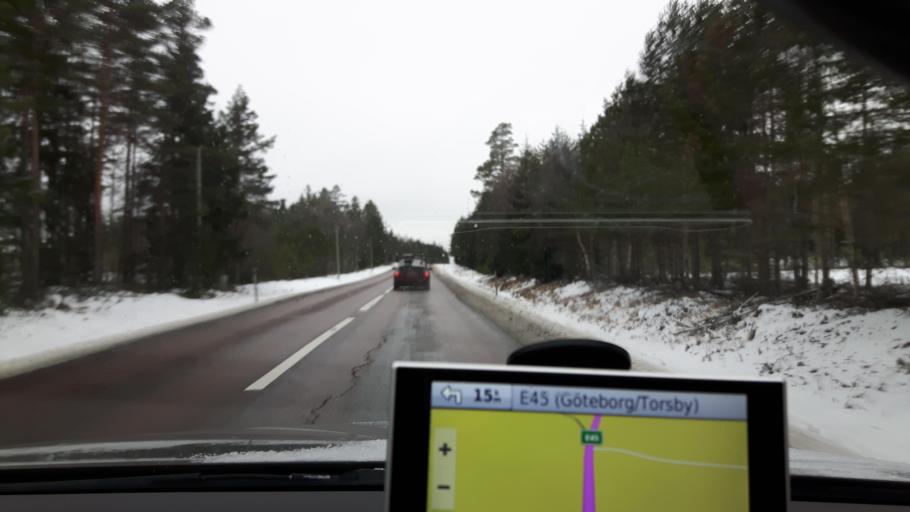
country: SE
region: Vaermland
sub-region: Torsby Kommun
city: Torsby
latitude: 60.3758
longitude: 13.2171
